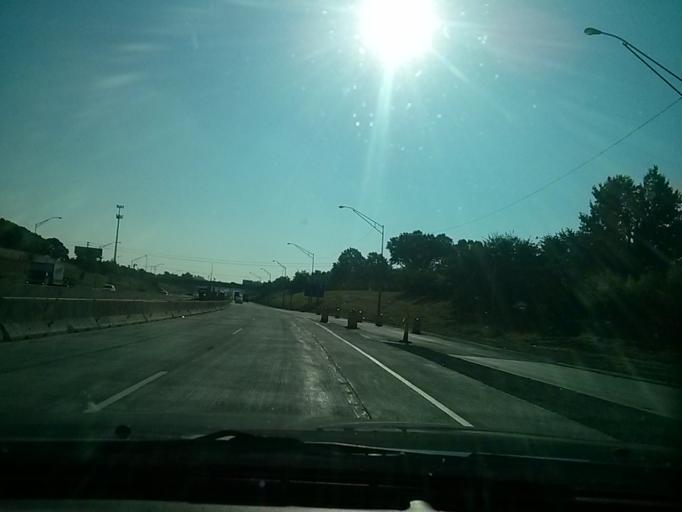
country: US
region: Oklahoma
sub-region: Tulsa County
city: Tulsa
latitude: 36.1592
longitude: -95.9439
